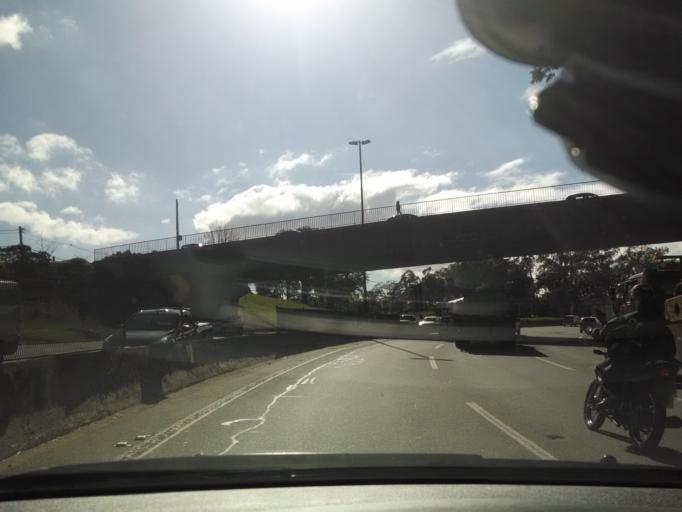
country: BR
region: Sao Paulo
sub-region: Taboao Da Serra
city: Taboao da Serra
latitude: -23.5896
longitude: -46.8306
